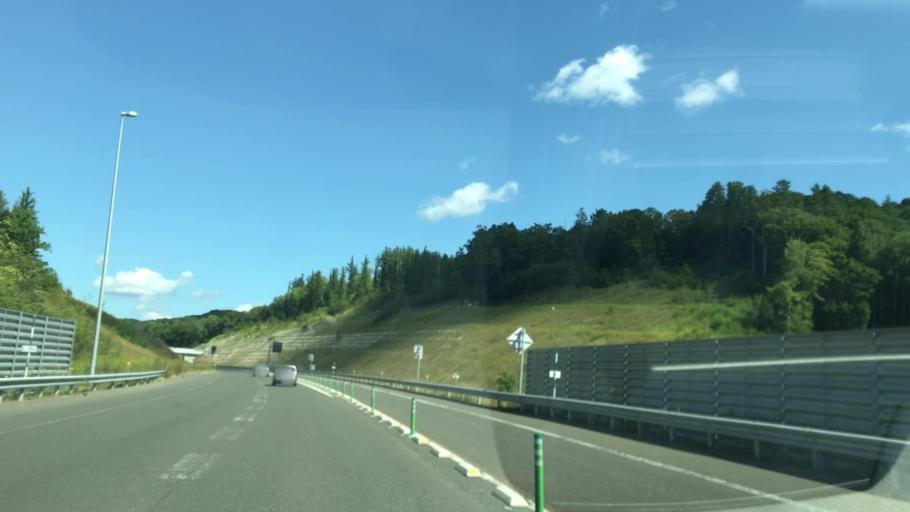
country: JP
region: Hokkaido
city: Shimo-furano
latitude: 42.9796
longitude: 142.4093
